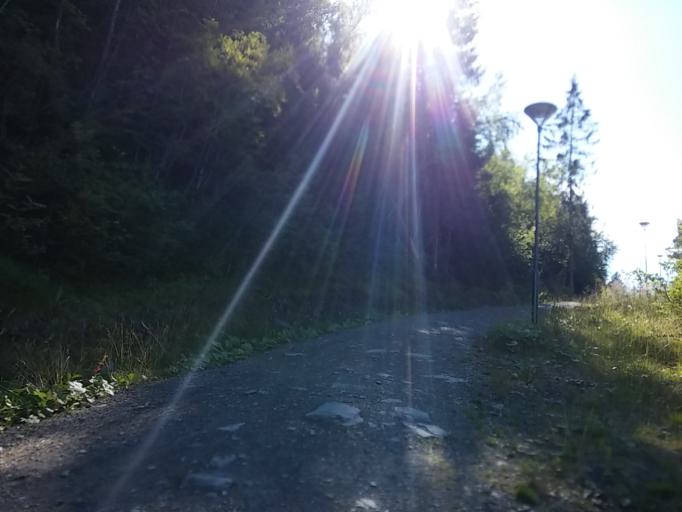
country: NO
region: Sor-Trondelag
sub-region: Malvik
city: Hommelvik
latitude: 63.4303
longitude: 10.7550
